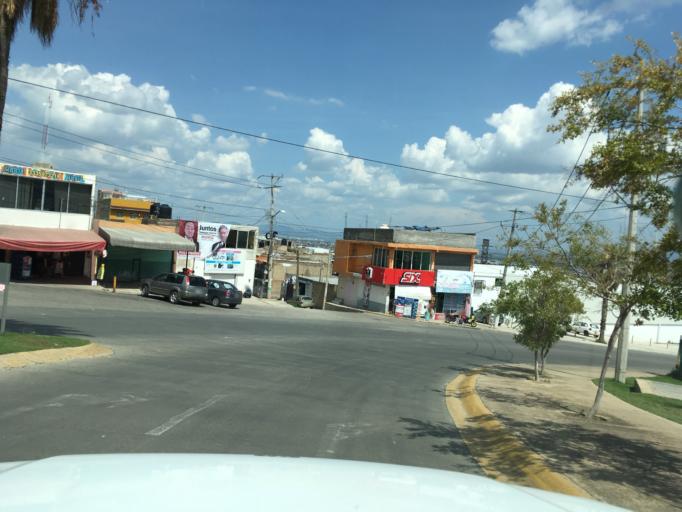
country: MX
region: Jalisco
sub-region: Tlajomulco de Zuniga
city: Altus Bosques
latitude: 20.5875
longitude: -103.3590
